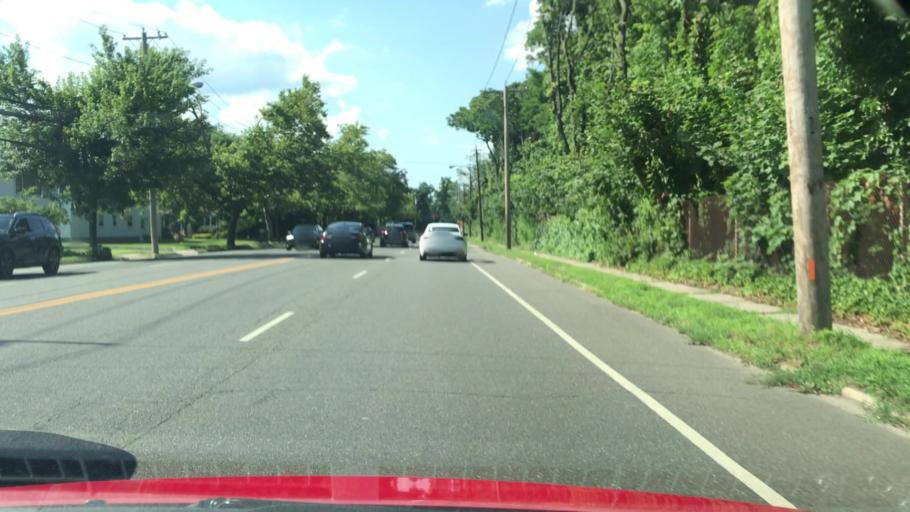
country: US
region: New York
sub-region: Nassau County
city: Malverne
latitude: 40.6743
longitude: -73.6632
